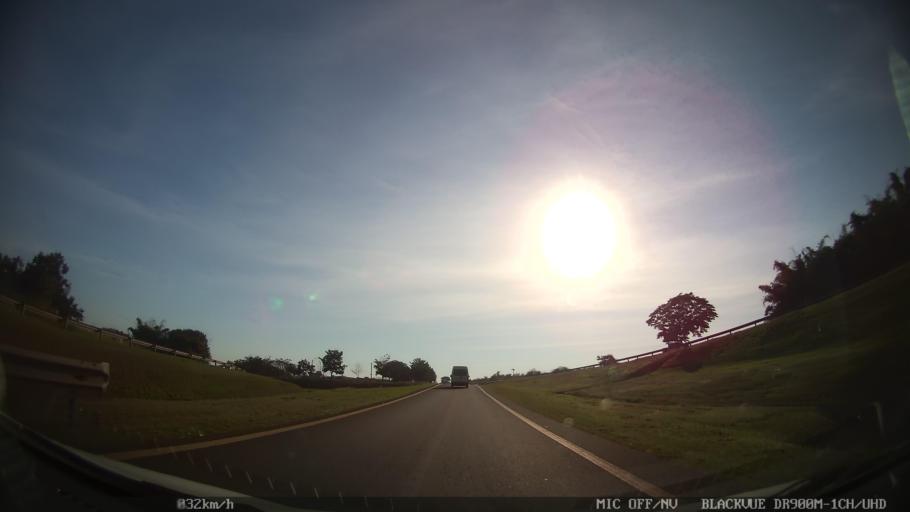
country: BR
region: Sao Paulo
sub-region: Cravinhos
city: Cravinhos
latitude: -21.2912
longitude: -47.8124
